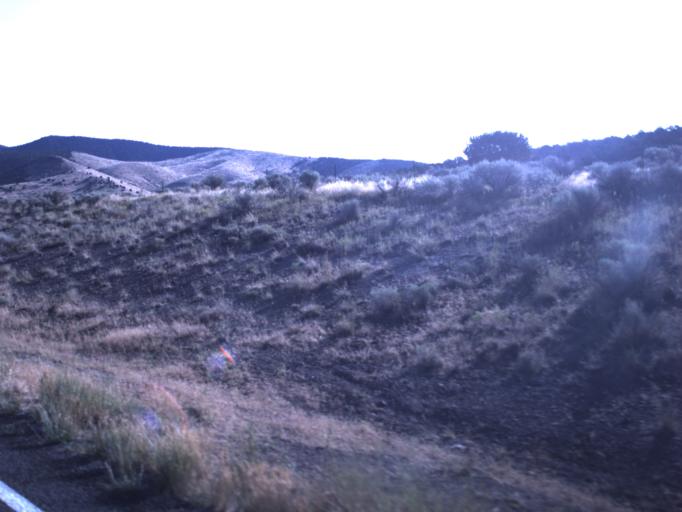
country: US
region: Utah
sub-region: Iron County
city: Parowan
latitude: 38.0930
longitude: -112.9507
